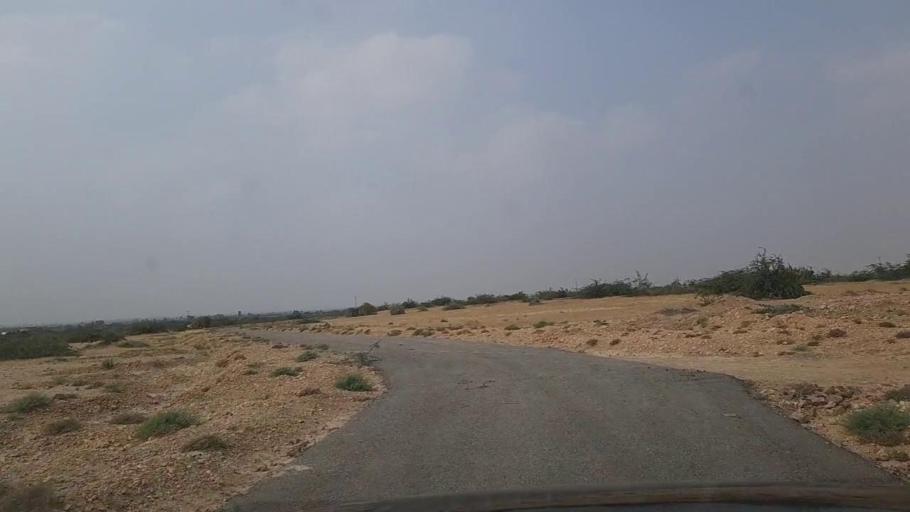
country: PK
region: Sindh
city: Thatta
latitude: 24.8048
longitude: 67.9160
